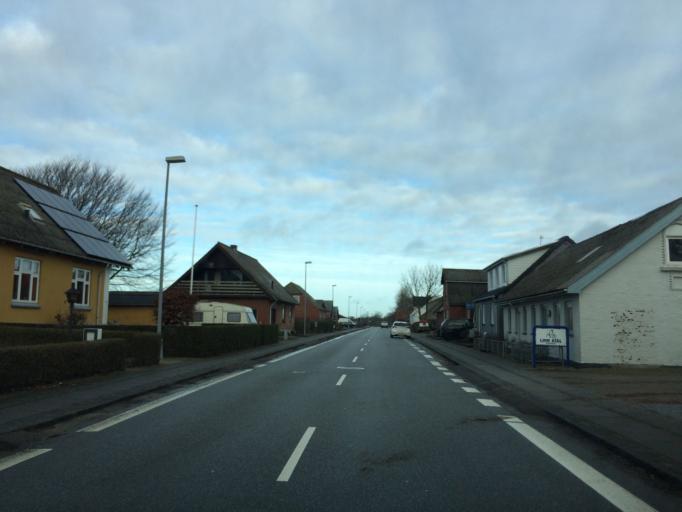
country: DK
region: Central Jutland
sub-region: Struer Kommune
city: Struer
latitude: 56.4716
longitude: 8.5482
